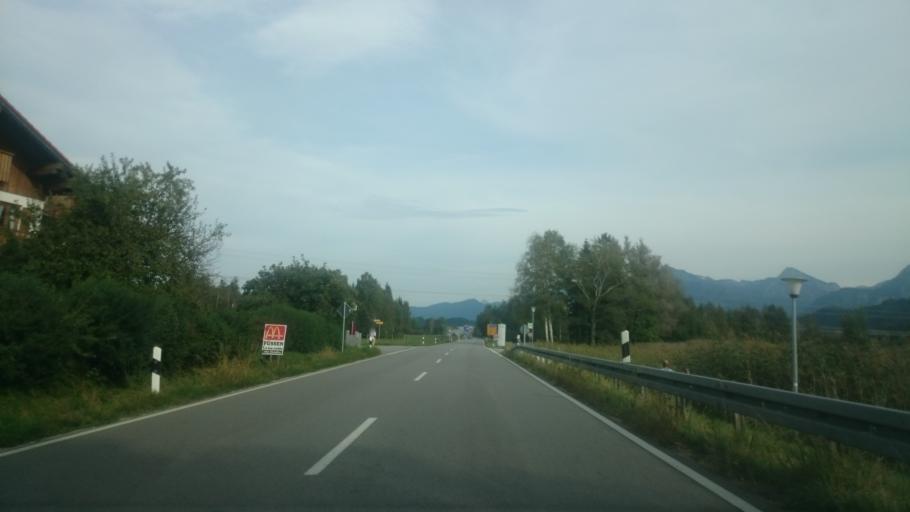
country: AT
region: Tyrol
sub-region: Politischer Bezirk Reutte
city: Vils
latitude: 47.5726
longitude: 10.6476
